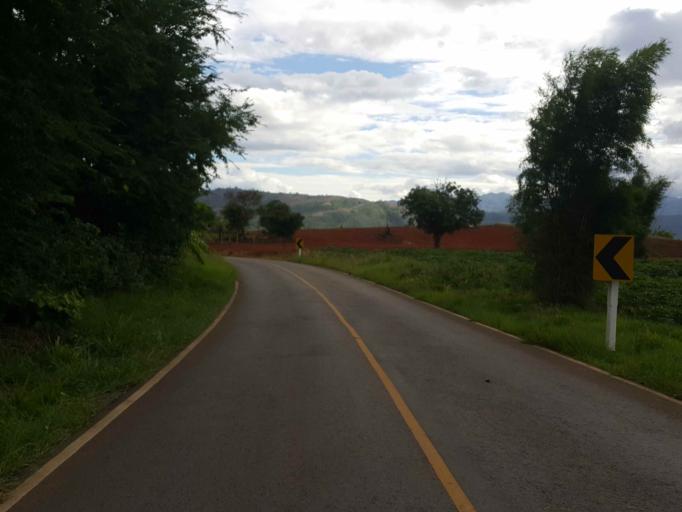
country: TH
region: Chiang Mai
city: Mae Chaem
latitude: 18.4974
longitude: 98.3899
